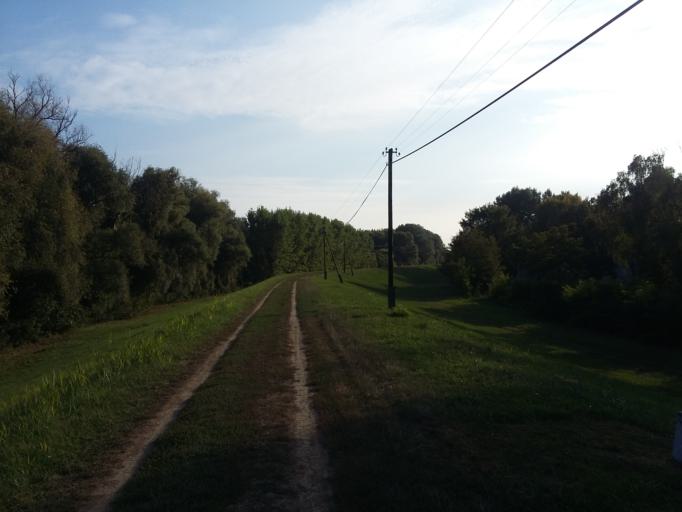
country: HU
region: Csongrad
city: Szeged
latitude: 46.2064
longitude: 20.1172
